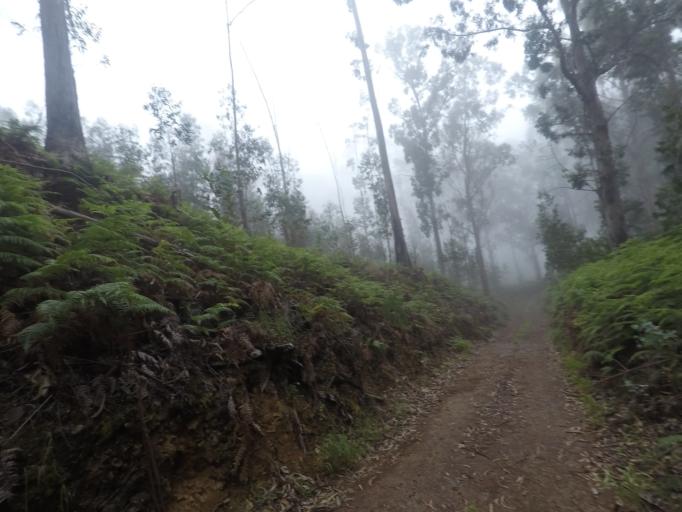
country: PT
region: Madeira
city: Ponta do Sol
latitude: 32.7203
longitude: -17.0924
